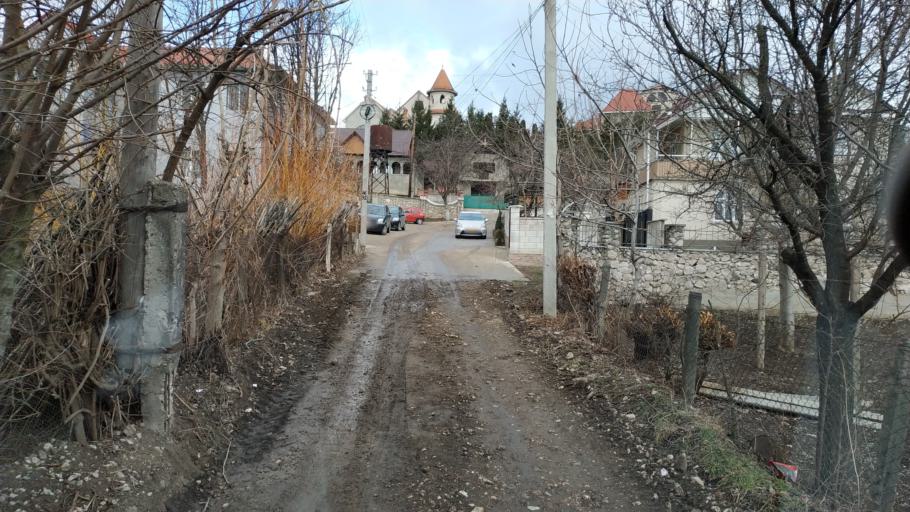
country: MD
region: Stinga Nistrului
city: Bucovat
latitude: 47.1556
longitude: 28.5221
